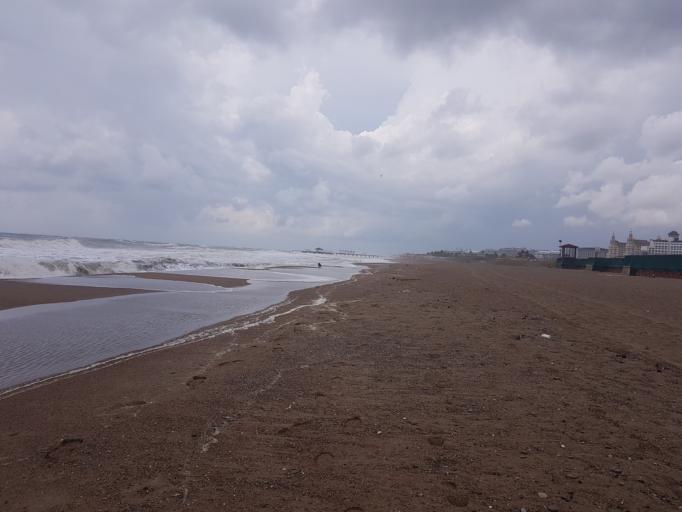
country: TR
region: Antalya
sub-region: Serik
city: Kumkoey
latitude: 36.8537
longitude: 30.9011
